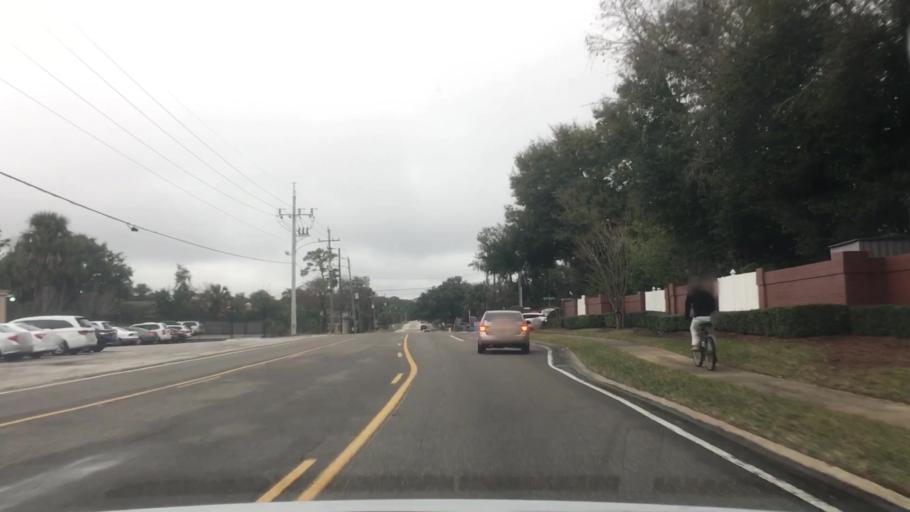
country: US
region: Florida
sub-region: Duval County
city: Jacksonville
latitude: 30.3597
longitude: -81.5772
